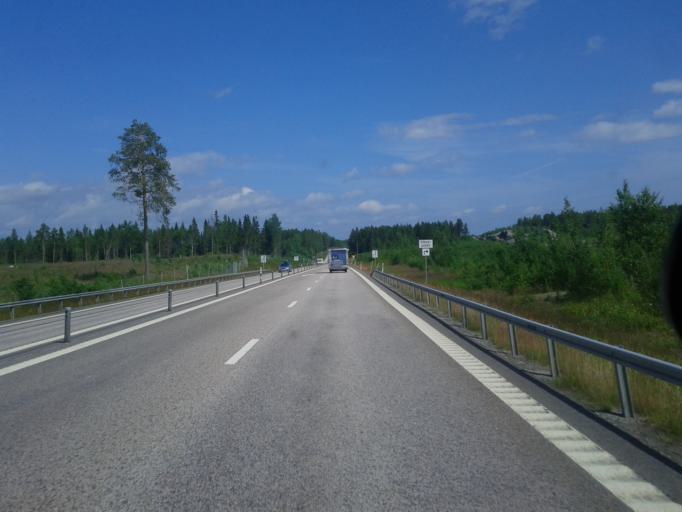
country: SE
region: Vaesterbotten
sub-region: Nordmalings Kommun
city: Nordmaling
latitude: 63.5087
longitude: 19.3526
